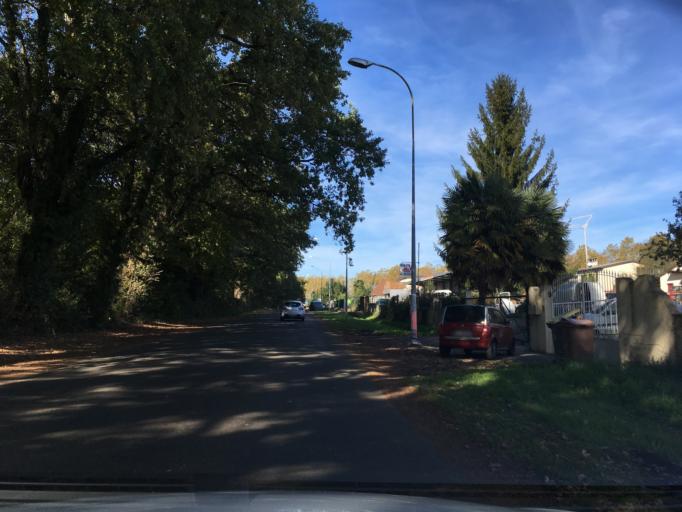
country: FR
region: Aquitaine
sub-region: Departement des Pyrenees-Atlantiques
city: Buros
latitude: 43.3214
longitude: -0.3166
